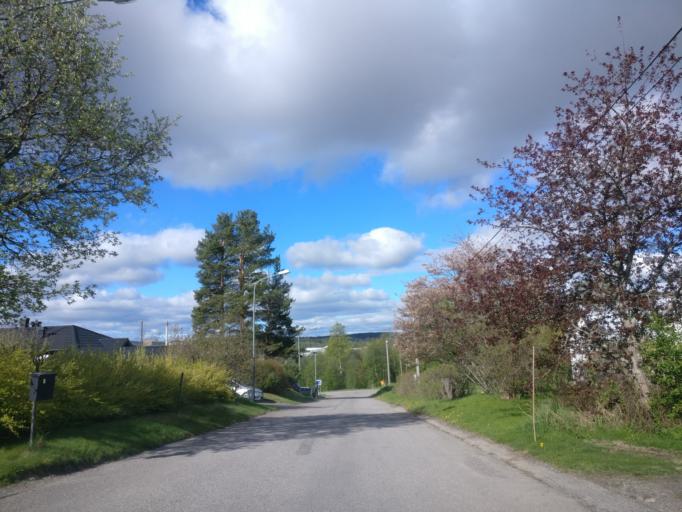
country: SE
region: Vaesternorrland
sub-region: Sundsvalls Kommun
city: Johannedal
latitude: 62.4124
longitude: 17.4167
